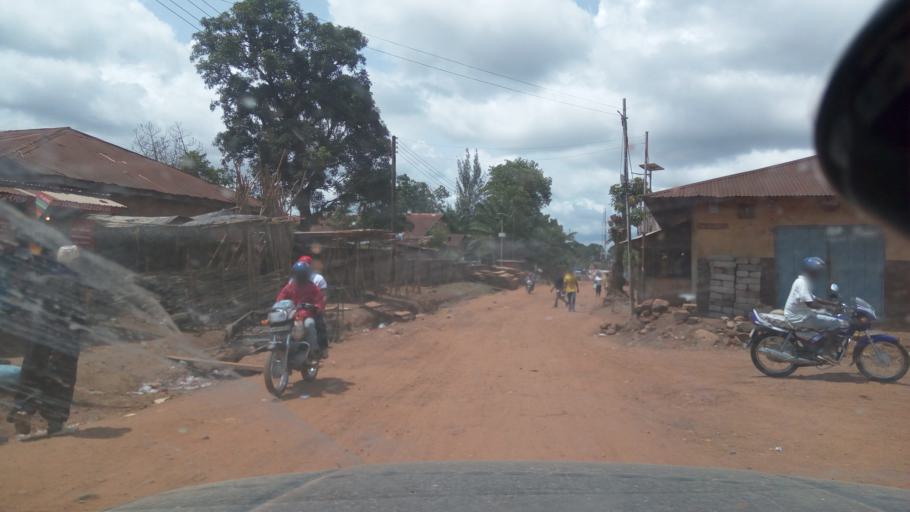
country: SL
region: Eastern Province
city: Kenema
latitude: 7.8784
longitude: -11.1888
